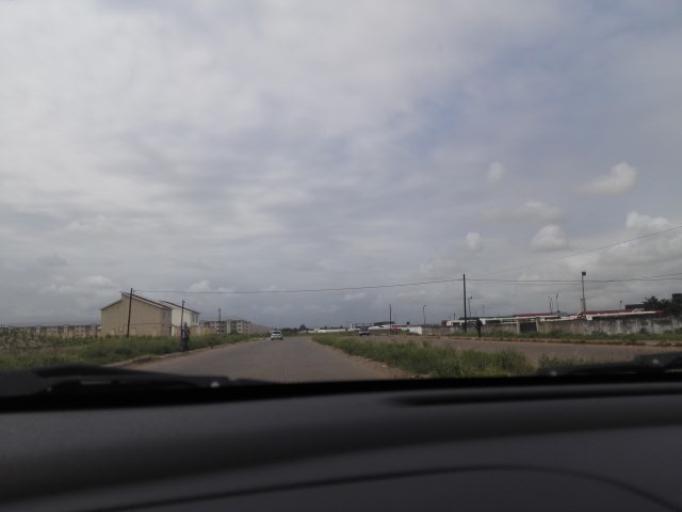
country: MZ
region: Maputo City
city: Maputo
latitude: -25.8220
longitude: 32.5827
